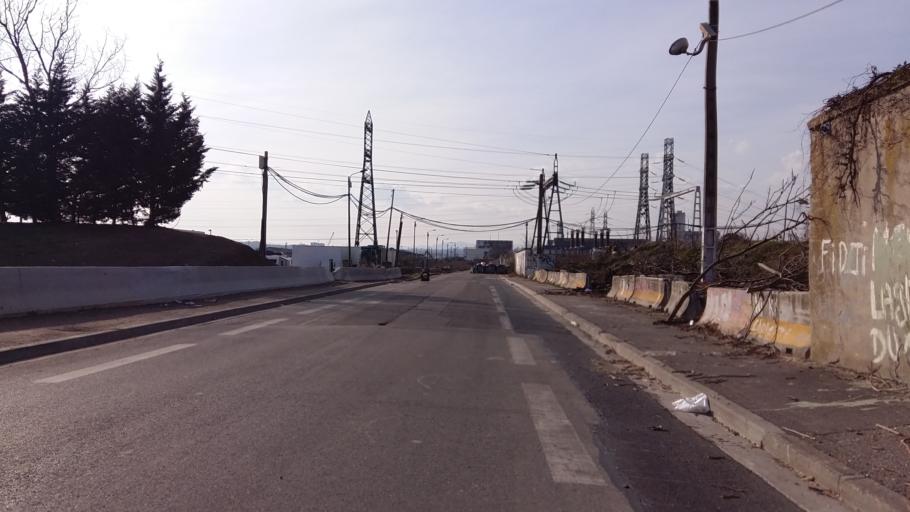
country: FR
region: Rhone-Alpes
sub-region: Departement du Rhone
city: Saint-Fons
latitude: 45.7191
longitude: 4.8472
